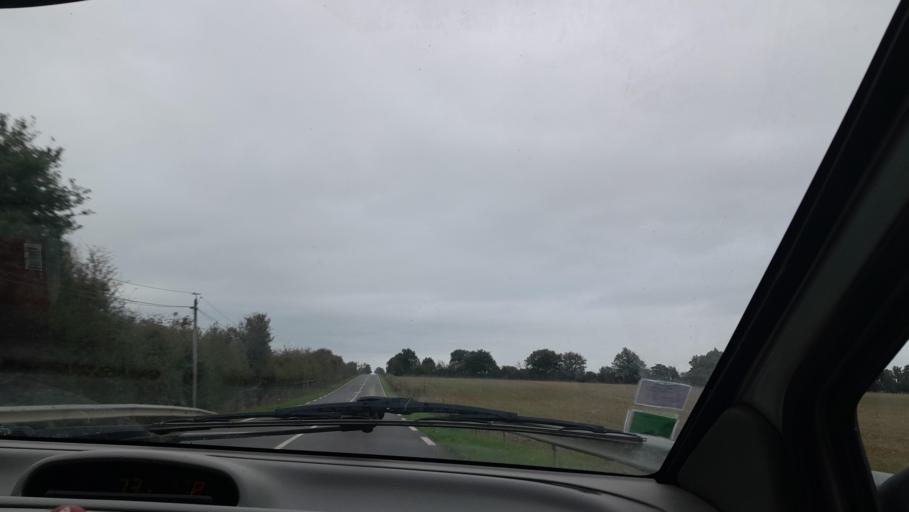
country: FR
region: Pays de la Loire
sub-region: Departement de la Loire-Atlantique
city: Saint-Mars-la-Jaille
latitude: 47.6288
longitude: -1.2003
